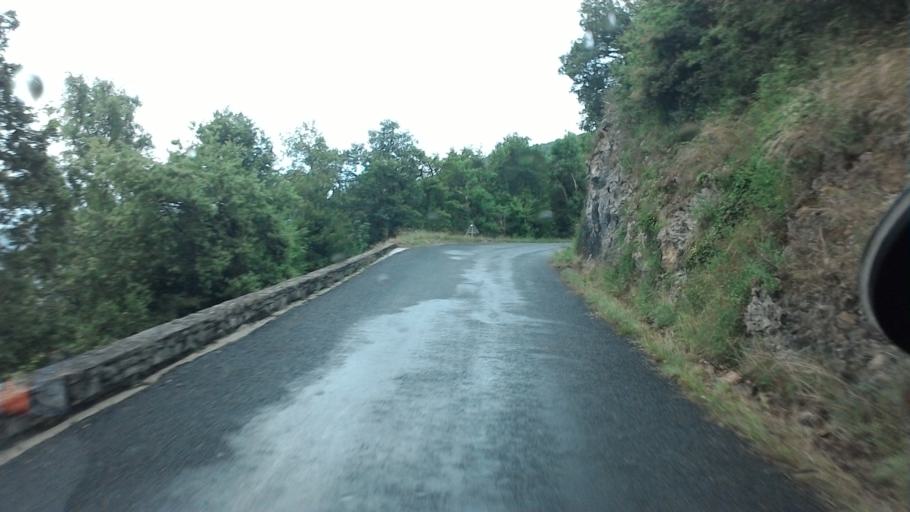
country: FR
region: Rhone-Alpes
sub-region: Departement de l'Ain
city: Belley
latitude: 45.7558
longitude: 5.5990
